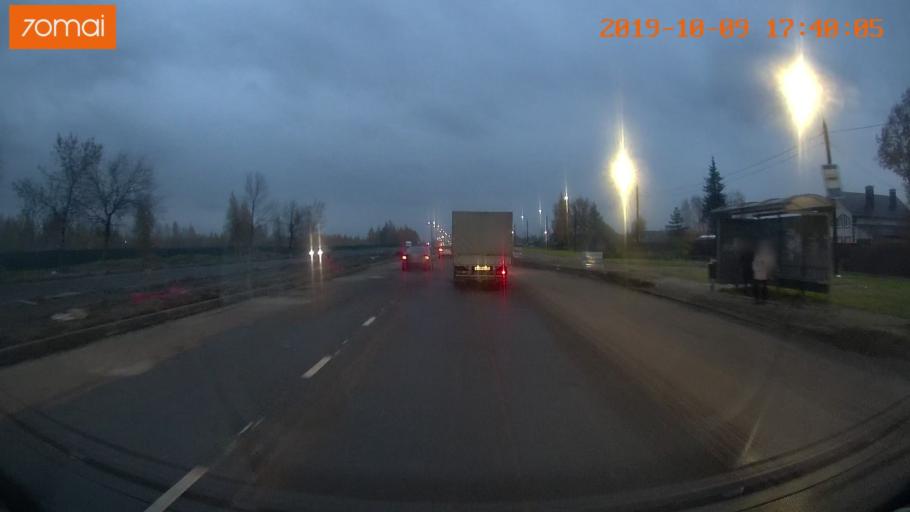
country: RU
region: Ivanovo
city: Bogorodskoye
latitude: 57.0576
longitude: 40.9629
